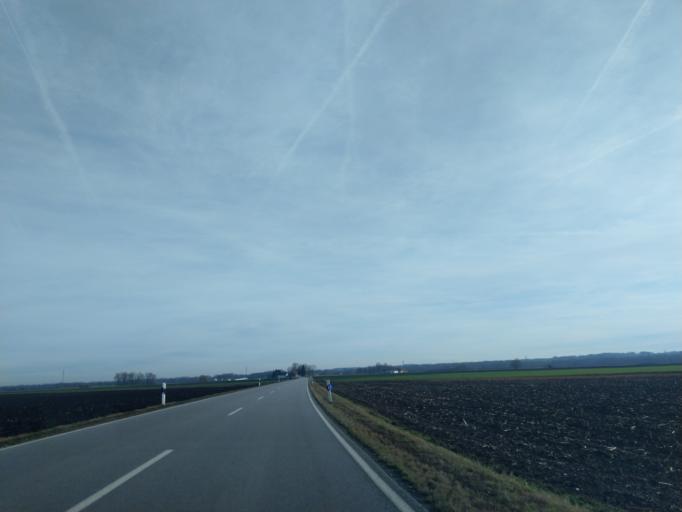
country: DE
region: Bavaria
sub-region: Lower Bavaria
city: Oberporing
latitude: 48.7229
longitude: 12.7879
